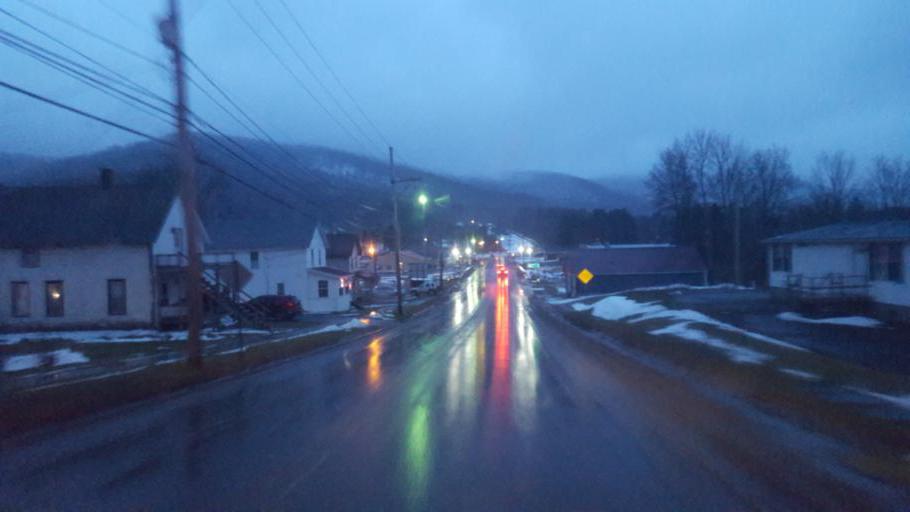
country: US
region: Pennsylvania
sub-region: McKean County
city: Smethport
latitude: 41.8085
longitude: -78.4518
